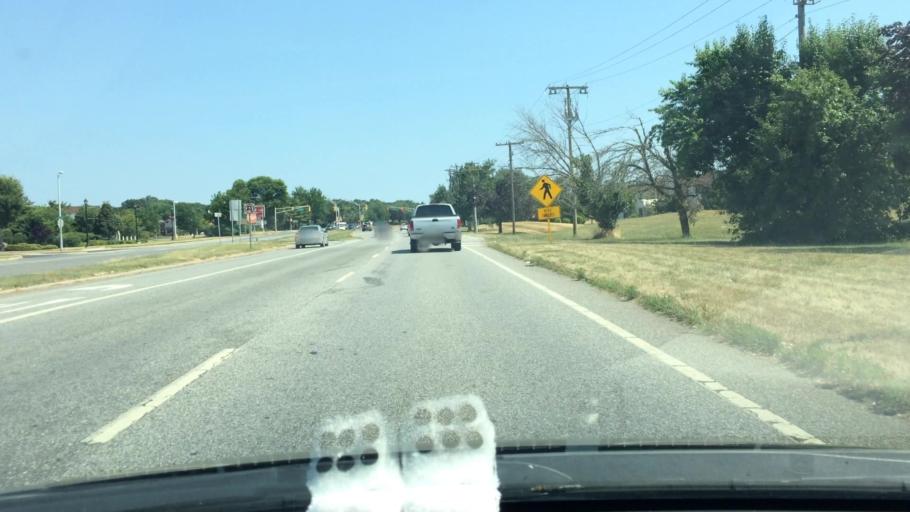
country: US
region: New Jersey
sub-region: Gloucester County
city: Beckett
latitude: 39.7589
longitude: -75.3579
